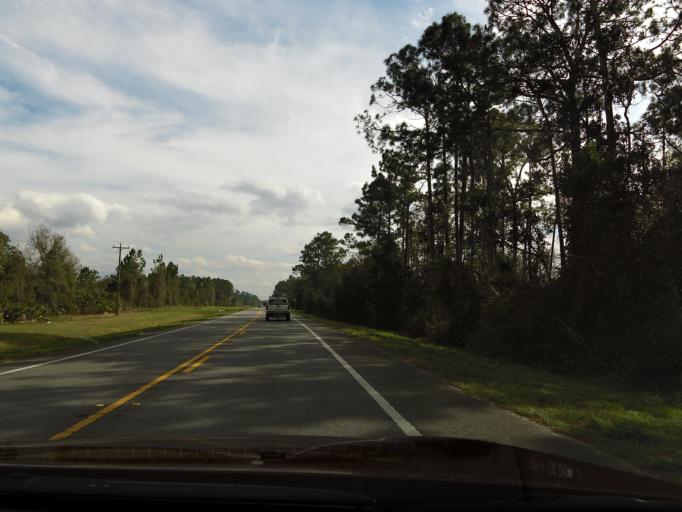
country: US
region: Florida
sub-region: Volusia County
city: De Leon Springs
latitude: 29.1944
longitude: -81.3128
